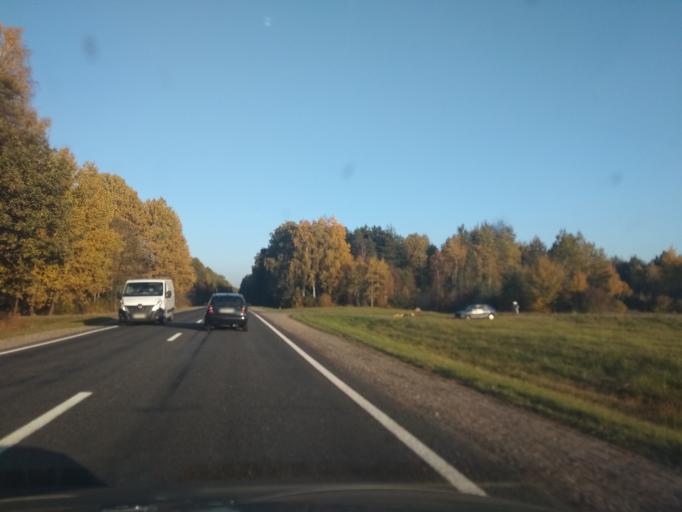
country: BY
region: Grodnenskaya
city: Zel'va
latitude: 53.1415
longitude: 24.6498
